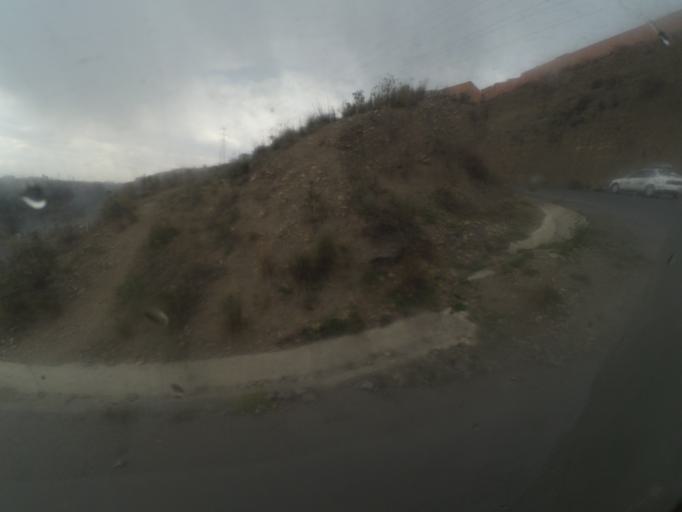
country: BO
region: La Paz
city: La Paz
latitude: -16.5567
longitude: -68.1759
